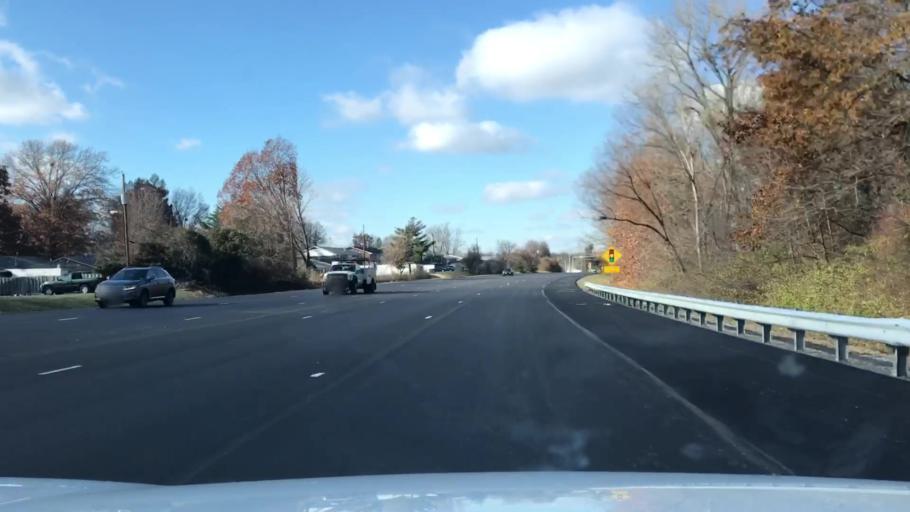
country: US
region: Illinois
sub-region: Saint Clair County
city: Swansea
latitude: 38.5534
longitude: -90.0160
